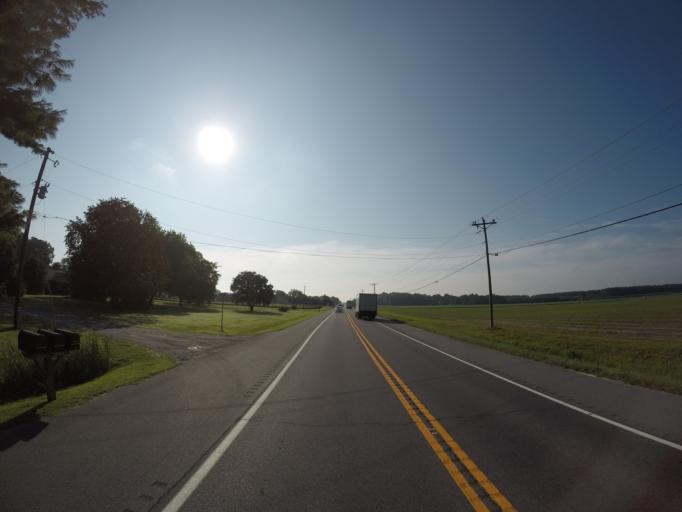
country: US
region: Delaware
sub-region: Sussex County
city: Bridgeville
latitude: 38.7079
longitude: -75.5196
